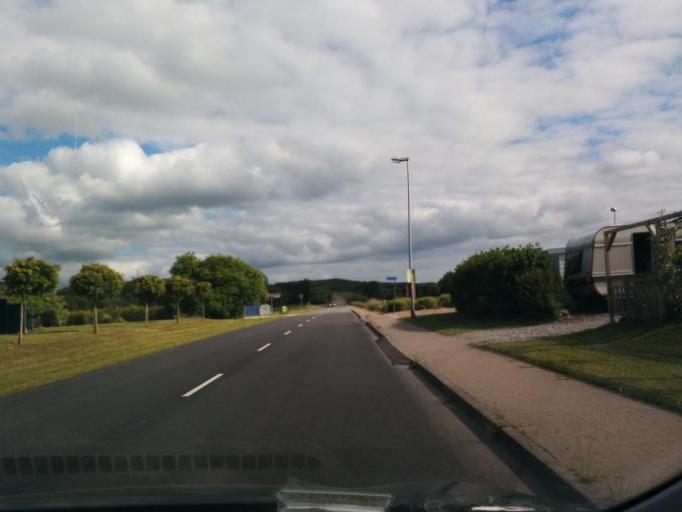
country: DK
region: Central Jutland
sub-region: Norddjurs Kommune
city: Grenaa
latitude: 56.5266
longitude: 10.7118
